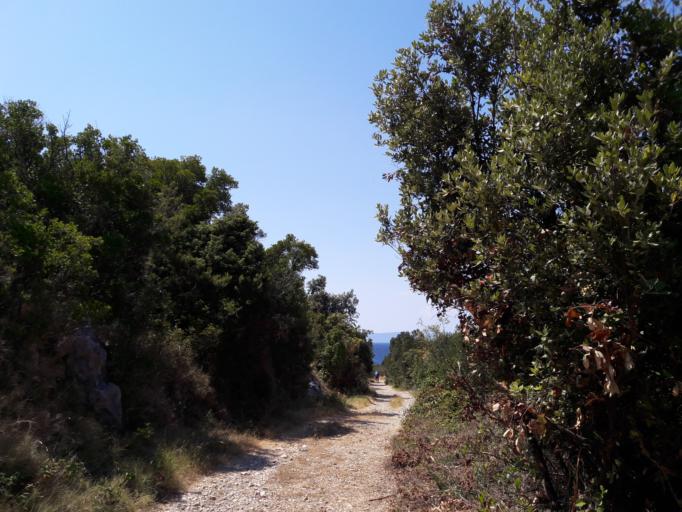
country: HR
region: Dubrovacko-Neretvanska
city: Orebic
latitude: 43.0219
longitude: 17.1648
